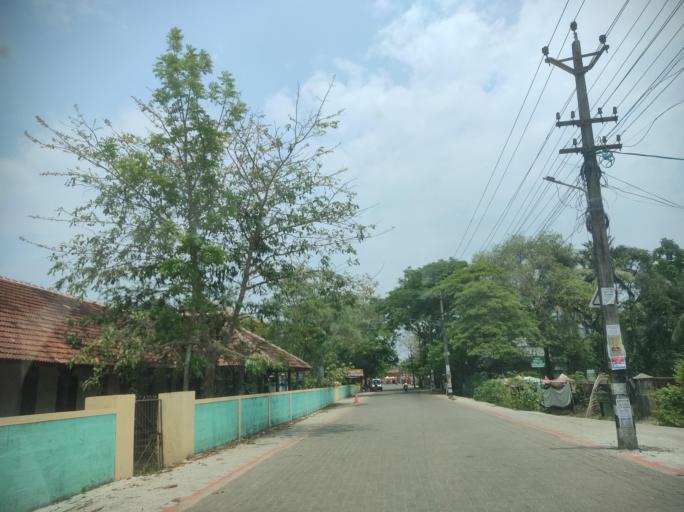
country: IN
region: Kerala
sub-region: Alappuzha
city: Vayalar
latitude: 9.7068
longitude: 76.3258
